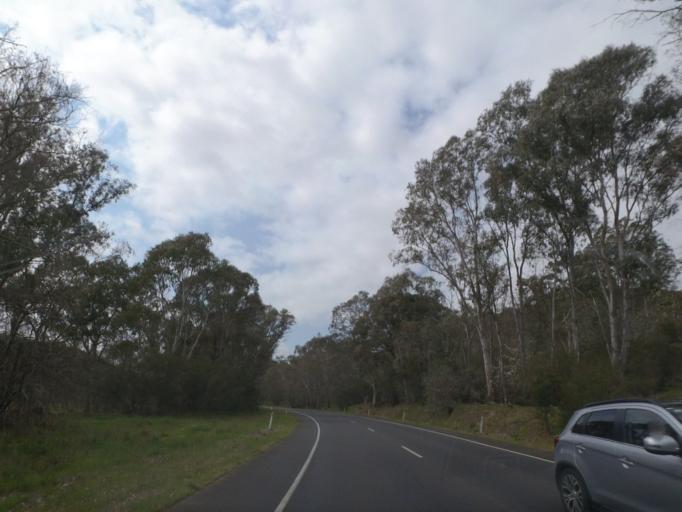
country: AU
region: Victoria
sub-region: Murrindindi
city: Kinglake West
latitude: -37.1447
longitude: 145.2466
